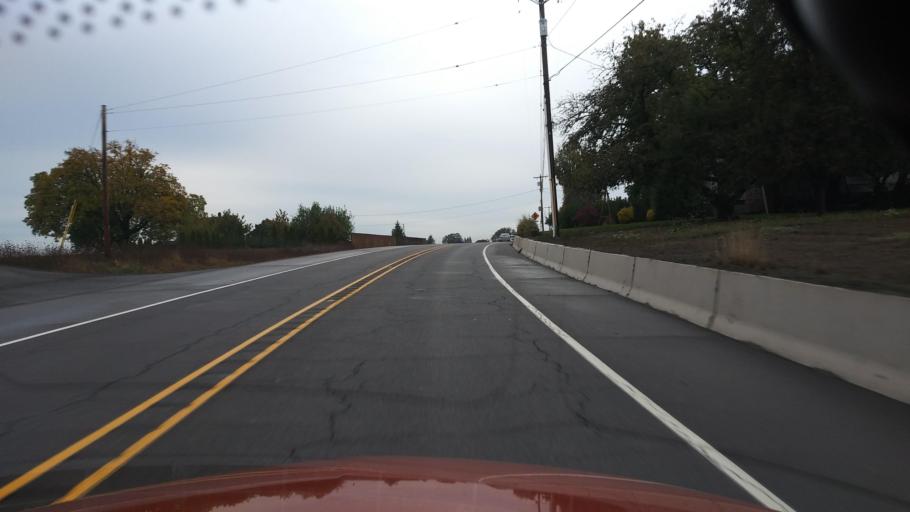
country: US
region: Oregon
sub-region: Washington County
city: Cornelius
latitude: 45.5307
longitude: -123.0594
